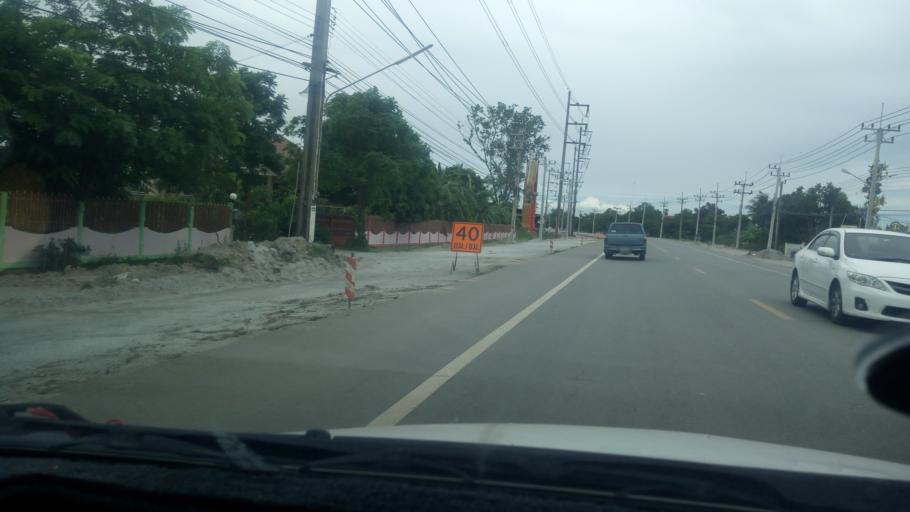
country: TH
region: Chon Buri
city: Phanat Nikhom
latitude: 13.5082
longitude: 101.1576
